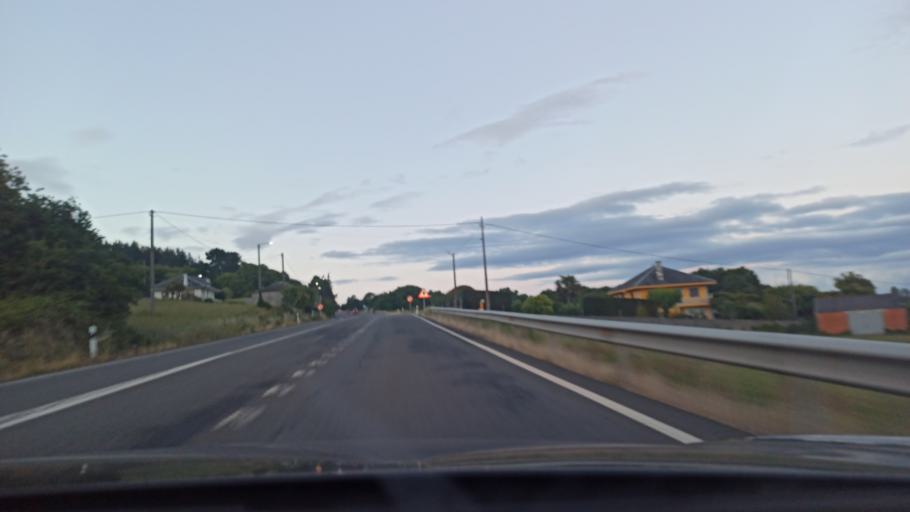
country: ES
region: Galicia
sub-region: Provincia de Lugo
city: Guntin
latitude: 42.9232
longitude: -7.6462
